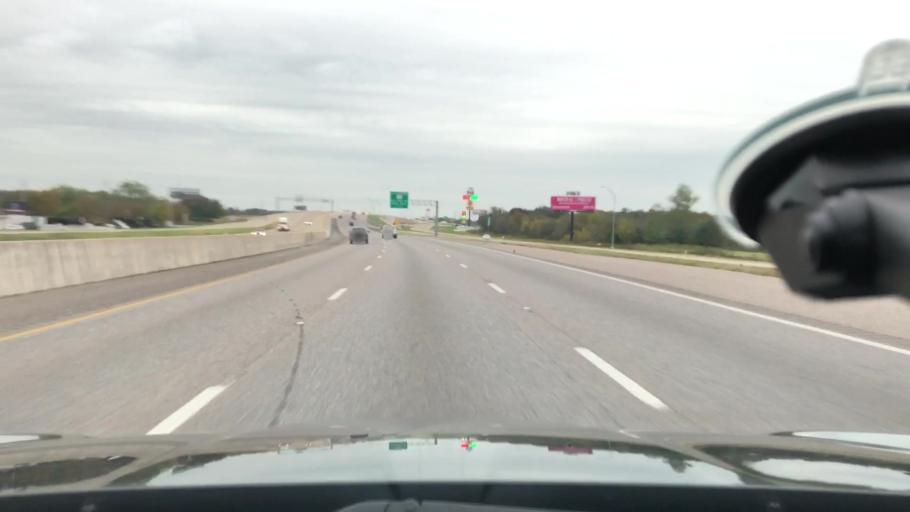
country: US
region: Texas
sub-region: McLennan County
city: Northcrest
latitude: 31.6451
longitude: -97.0972
